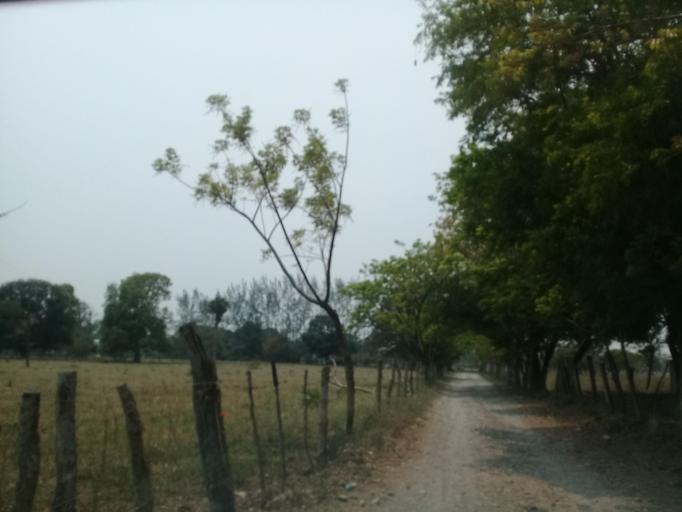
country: MX
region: Veracruz
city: Jamapa
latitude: 18.9325
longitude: -96.2131
